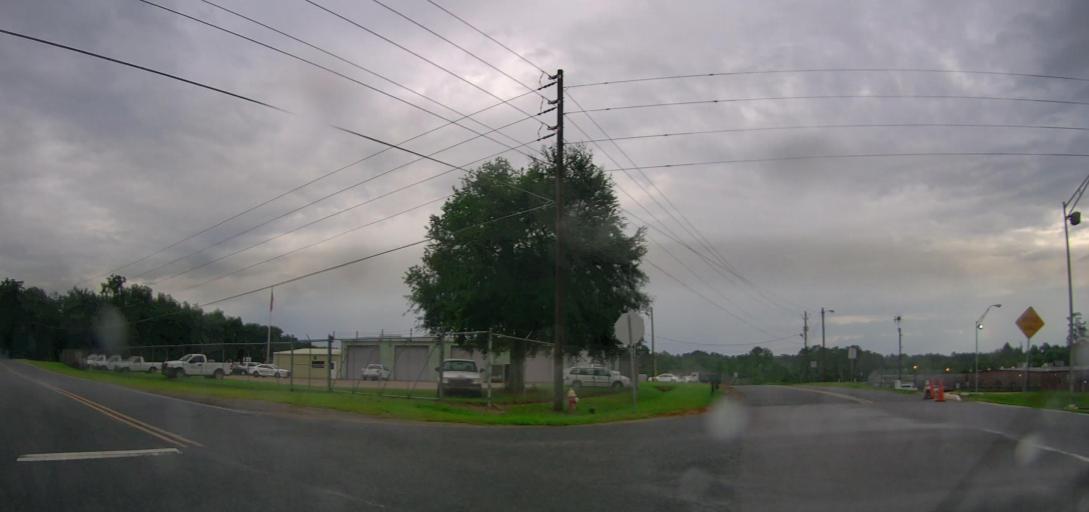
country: US
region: Georgia
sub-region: Ware County
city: Deenwood
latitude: 31.2577
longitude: -82.3916
